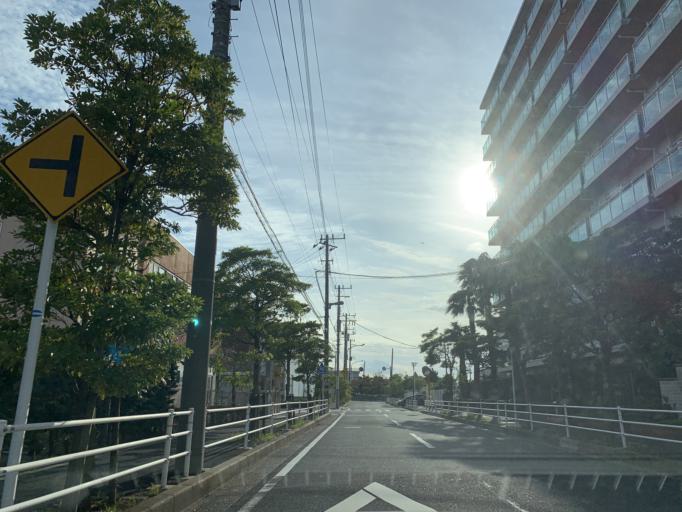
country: JP
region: Tokyo
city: Urayasu
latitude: 35.6391
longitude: 139.9105
